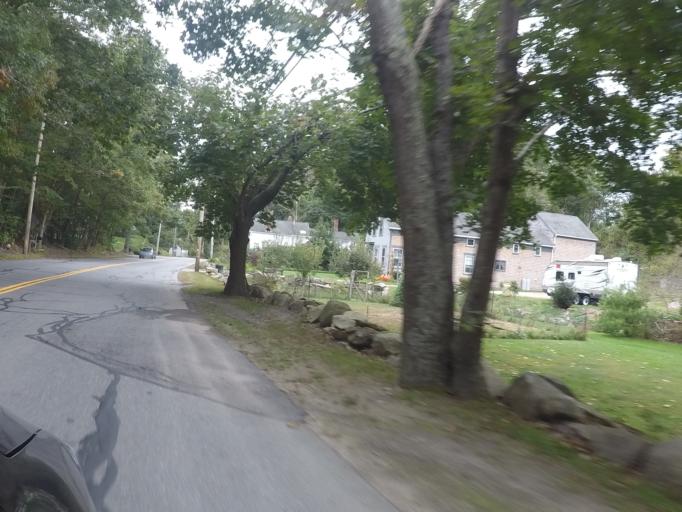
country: US
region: Massachusetts
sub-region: Bristol County
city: Smith Mills
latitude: 41.5776
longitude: -71.0032
